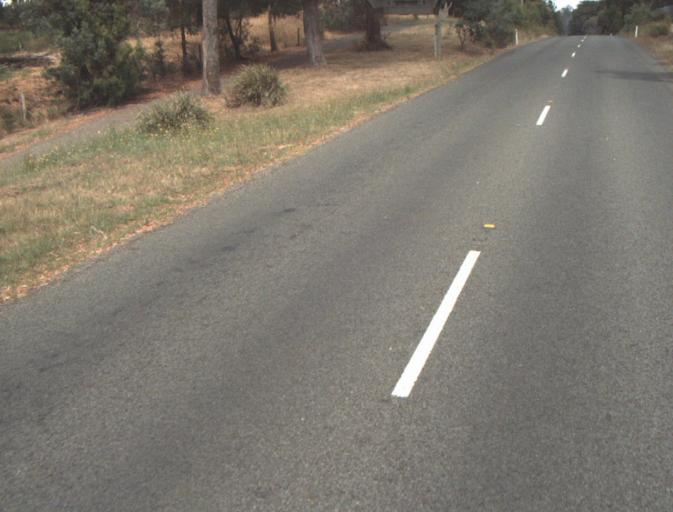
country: AU
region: Tasmania
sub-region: Launceston
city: Newstead
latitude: -41.4655
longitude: 147.1694
